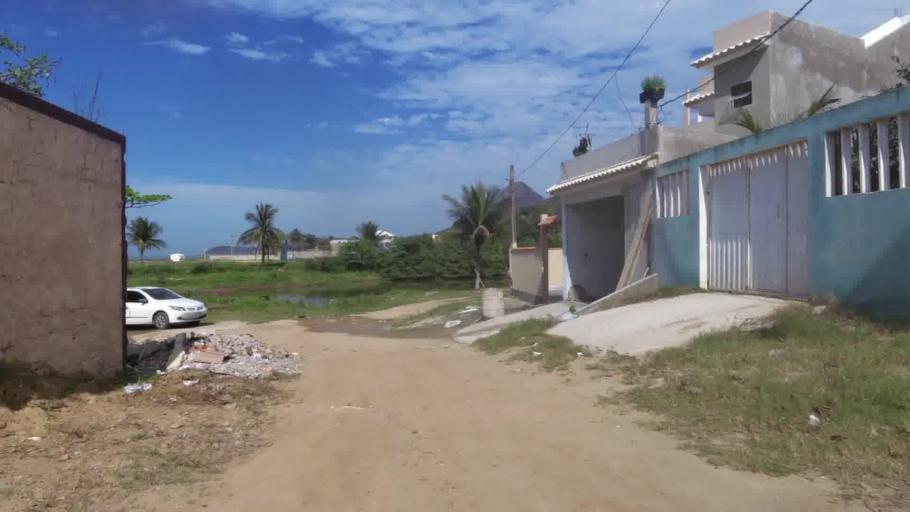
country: BR
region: Espirito Santo
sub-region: Piuma
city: Piuma
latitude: -20.8531
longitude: -40.7504
